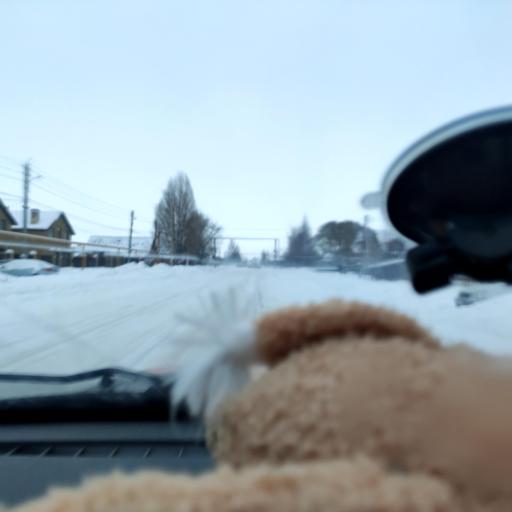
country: RU
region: Samara
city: Podstepki
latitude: 53.5133
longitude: 49.1821
